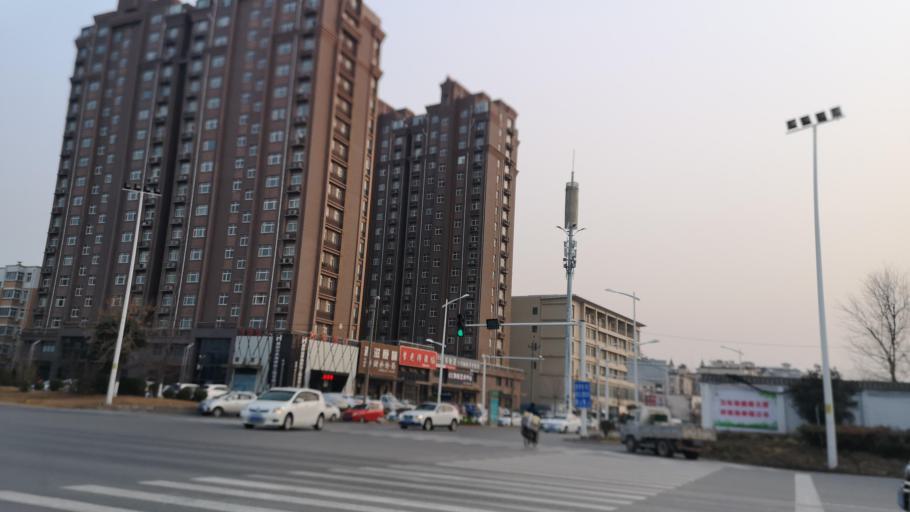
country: CN
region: Henan Sheng
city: Zhongyuanlu
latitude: 35.7895
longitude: 115.0821
